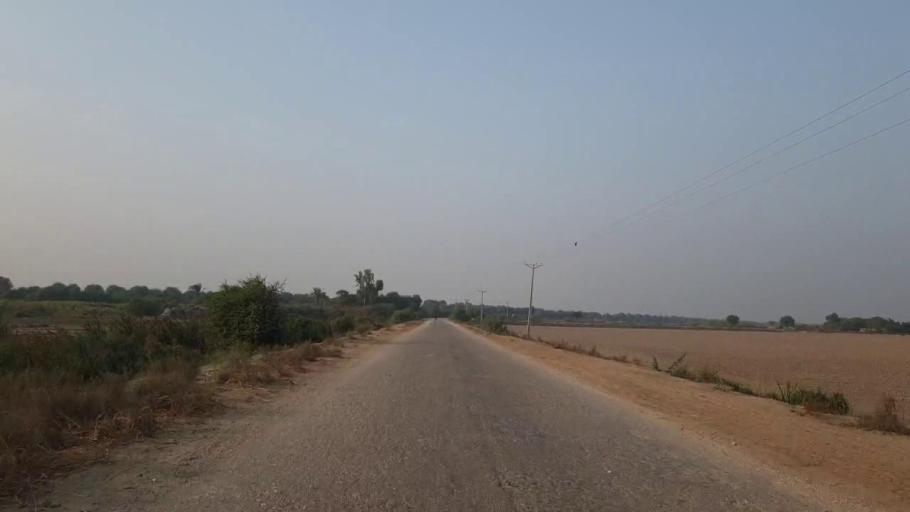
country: PK
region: Sindh
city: Tando Muhammad Khan
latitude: 25.1120
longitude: 68.4286
